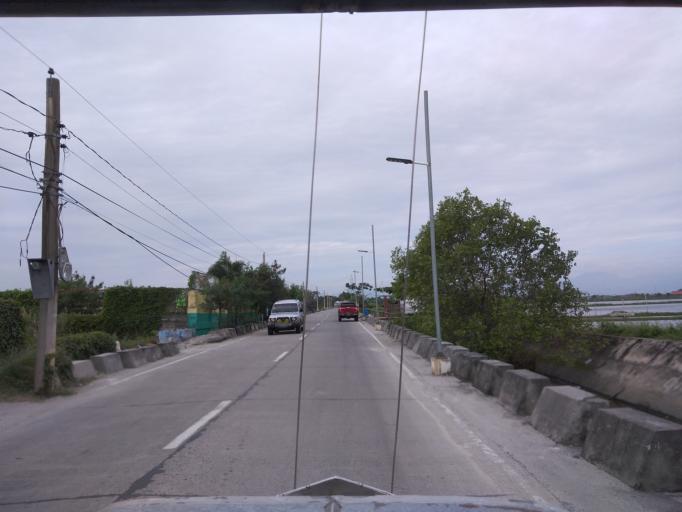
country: PH
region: Central Luzon
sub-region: Province of Pampanga
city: Sexmoan
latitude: 14.9370
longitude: 120.6182
